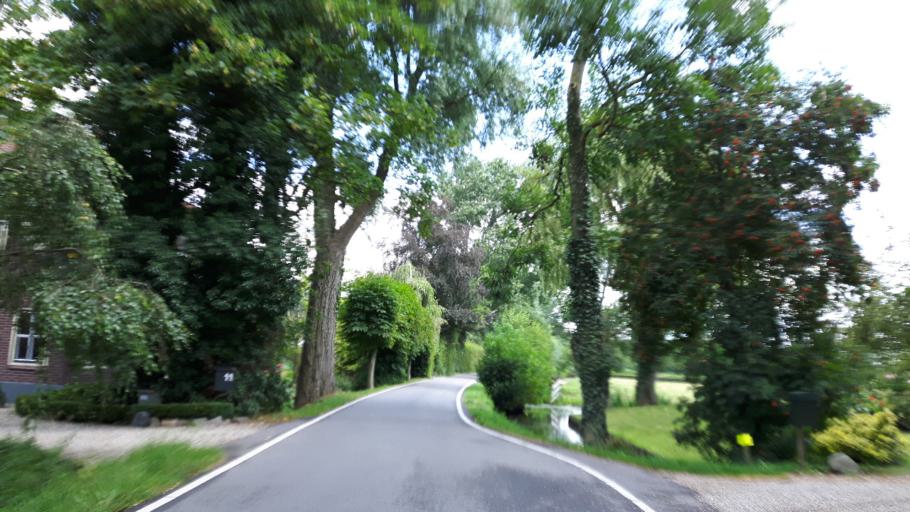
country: NL
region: Utrecht
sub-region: Gemeente Woerden
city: Woerden
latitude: 52.1001
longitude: 4.9173
